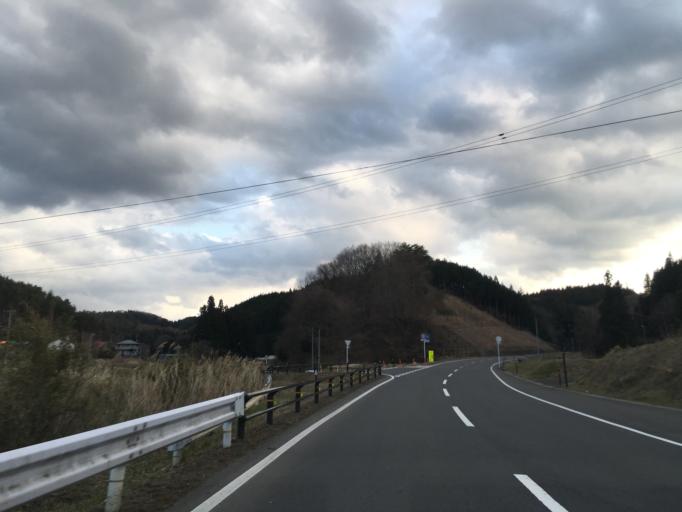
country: JP
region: Fukushima
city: Ishikawa
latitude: 37.0555
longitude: 140.5103
